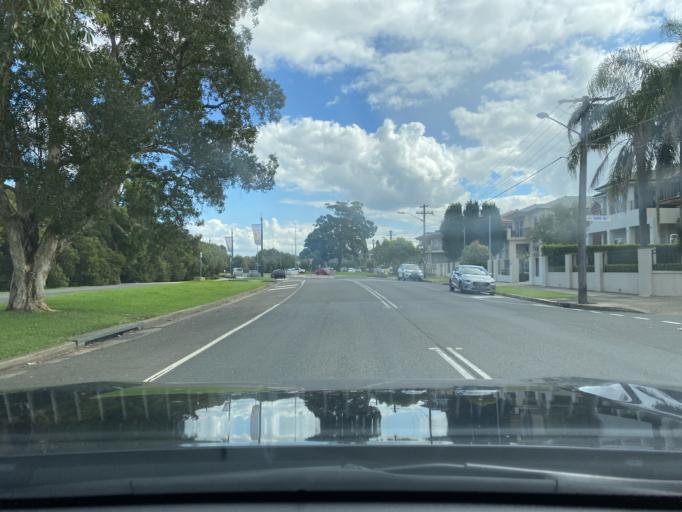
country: AU
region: New South Wales
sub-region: Canada Bay
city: Wareemba
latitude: -33.8679
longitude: 151.1426
